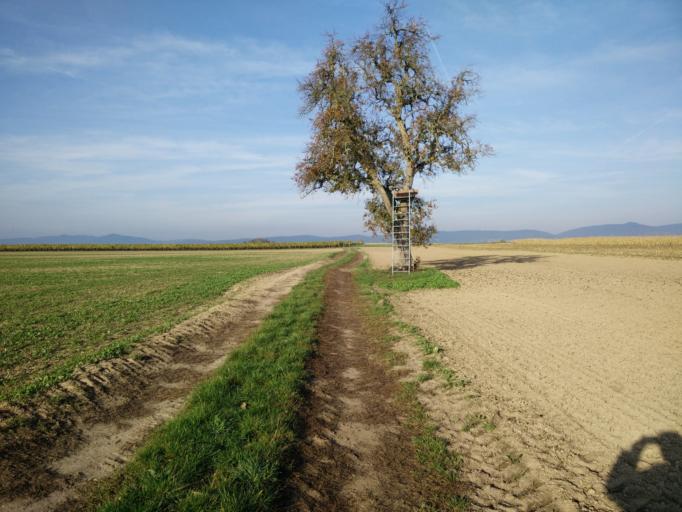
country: DE
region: Rheinland-Pfalz
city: Barbelroth
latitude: 49.1068
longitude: 8.0701
